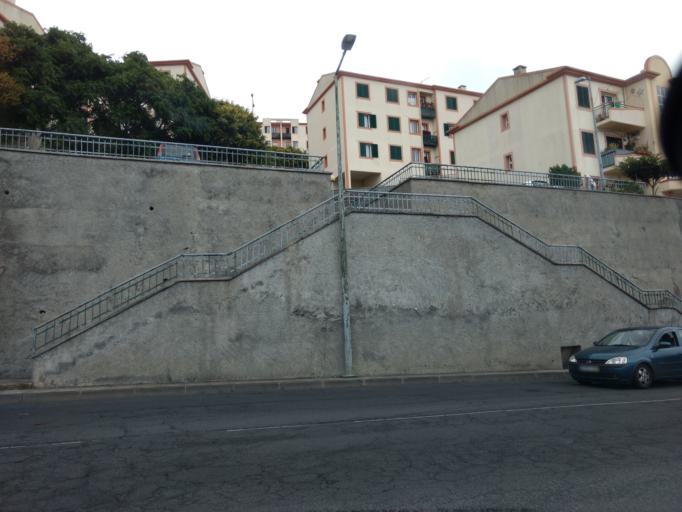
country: PT
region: Madeira
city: Camara de Lobos
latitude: 32.6627
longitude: -16.9486
